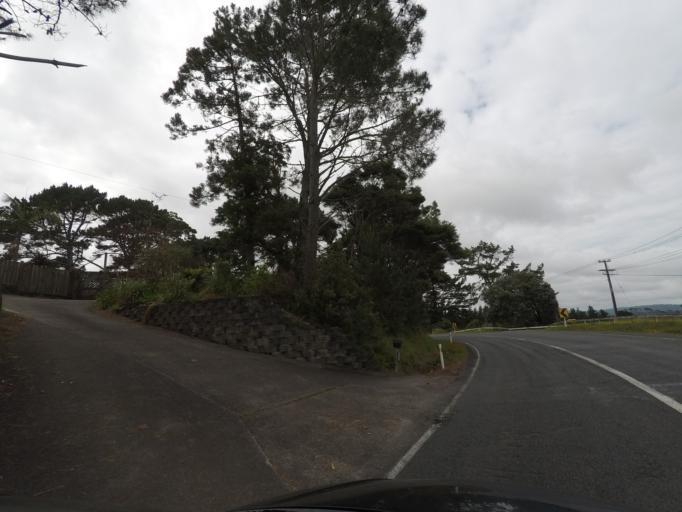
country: NZ
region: Auckland
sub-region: Auckland
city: Rosebank
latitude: -36.8311
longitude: 174.5749
